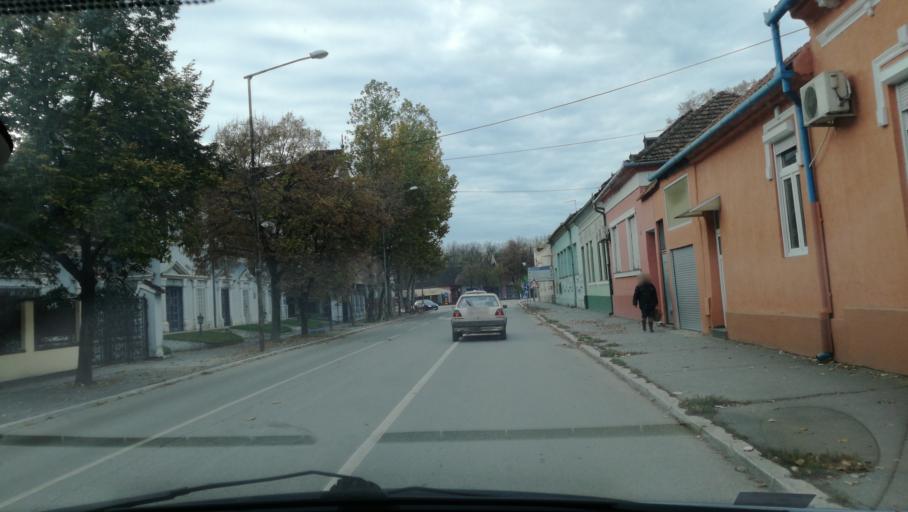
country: RS
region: Autonomna Pokrajina Vojvodina
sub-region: Severnobanatski Okrug
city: Kikinda
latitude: 45.8343
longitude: 20.4703
